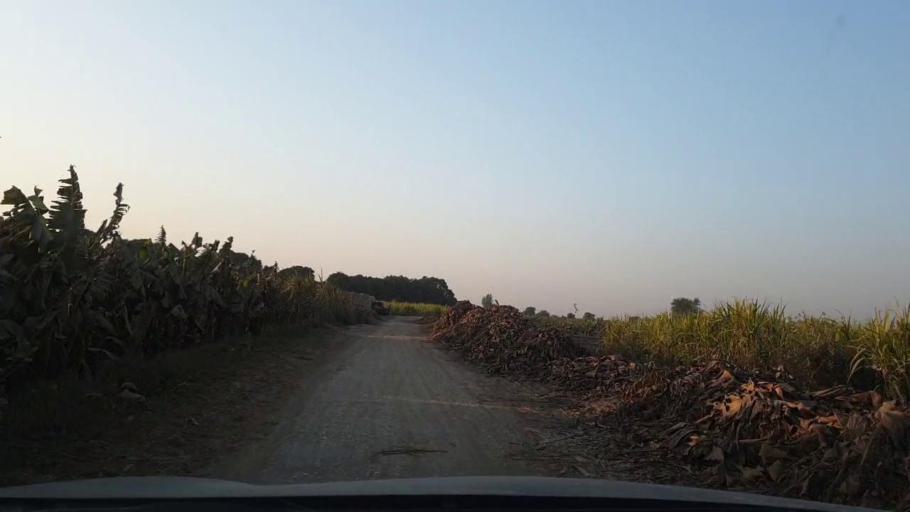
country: PK
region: Sindh
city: Tando Allahyar
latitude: 25.4957
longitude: 68.7414
